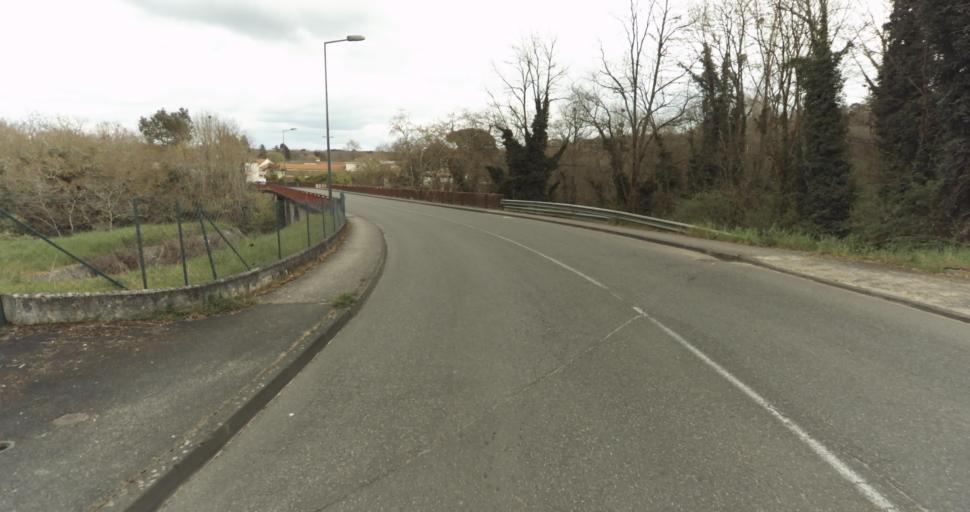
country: FR
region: Aquitaine
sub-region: Departement des Landes
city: Roquefort
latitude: 44.0312
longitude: -0.3247
